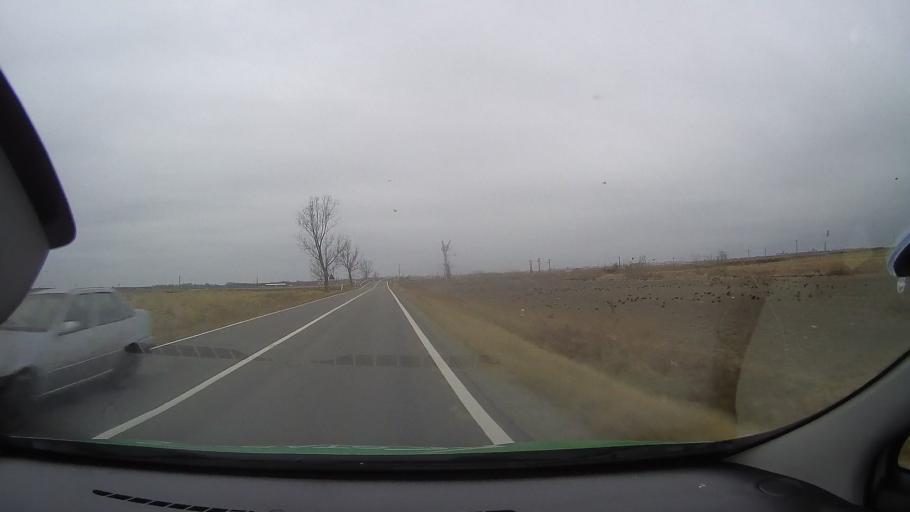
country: RO
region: Ialomita
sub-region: Comuna Slobozia
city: Slobozia
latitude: 44.5923
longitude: 27.3907
